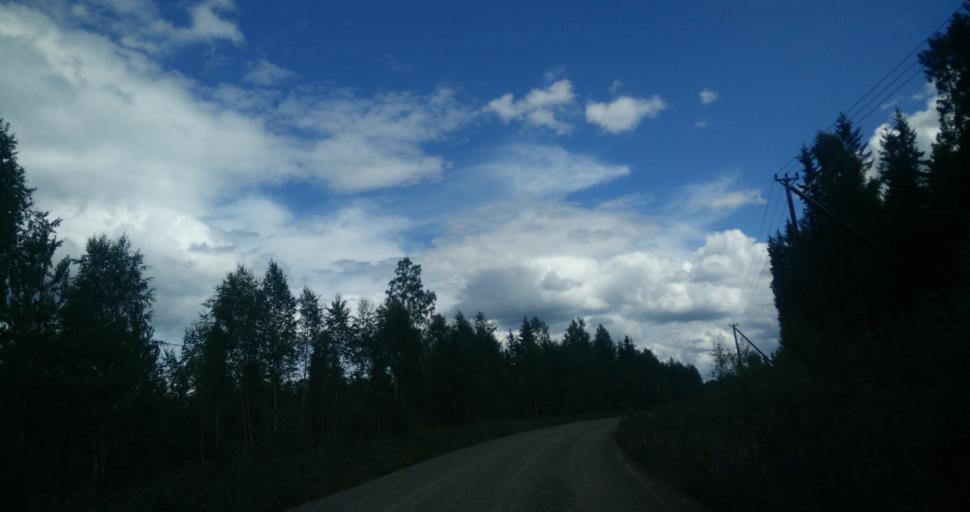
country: SE
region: Gaevleborg
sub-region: Nordanstigs Kommun
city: Bergsjoe
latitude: 62.0574
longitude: 16.8133
